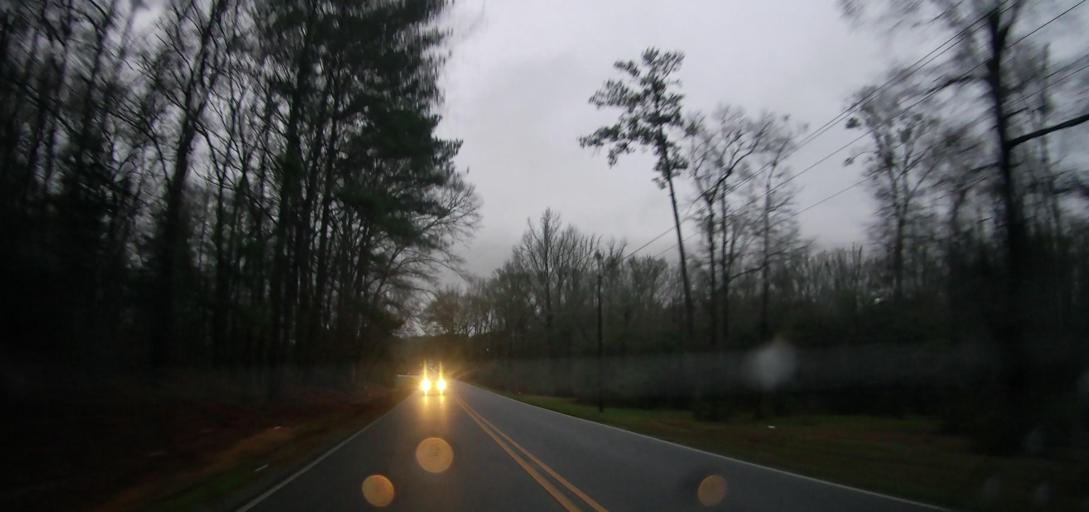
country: US
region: Alabama
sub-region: Tuscaloosa County
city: Vance
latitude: 33.1175
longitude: -87.2220
